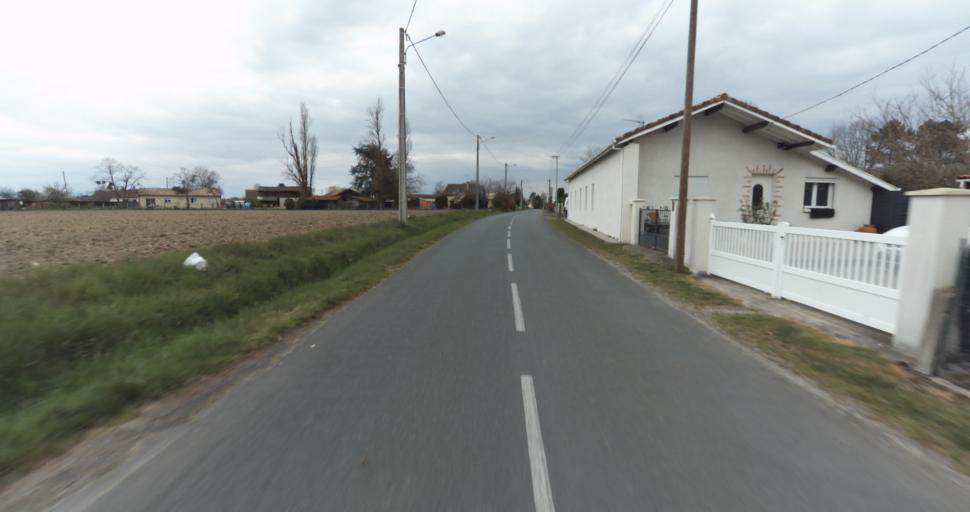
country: FR
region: Aquitaine
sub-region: Departement des Landes
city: Sarbazan
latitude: 44.0221
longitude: -0.3244
